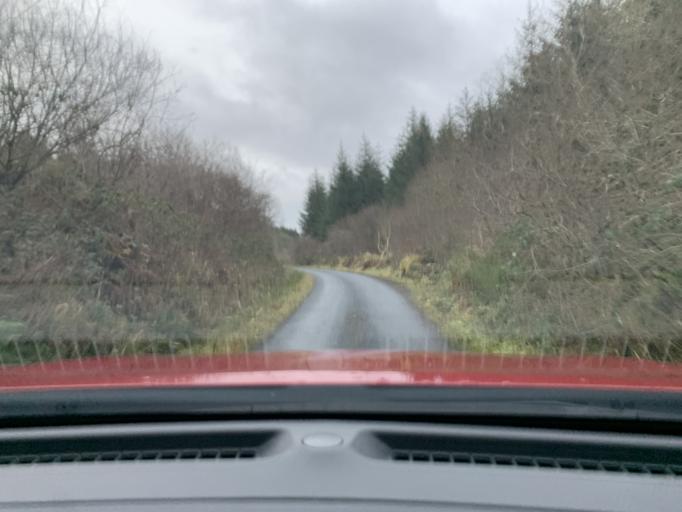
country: IE
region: Connaught
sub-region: Roscommon
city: Boyle
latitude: 54.0049
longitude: -8.3862
